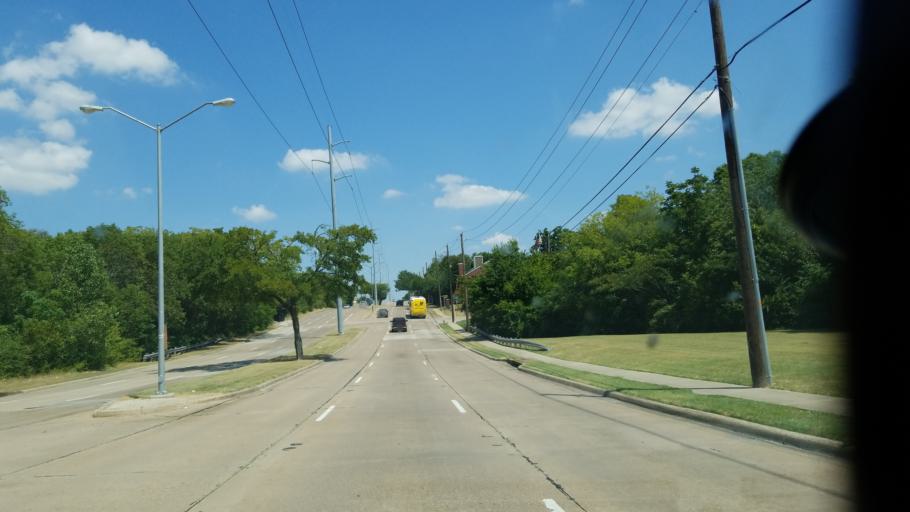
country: US
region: Texas
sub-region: Dallas County
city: Duncanville
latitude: 32.6733
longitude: -96.8827
